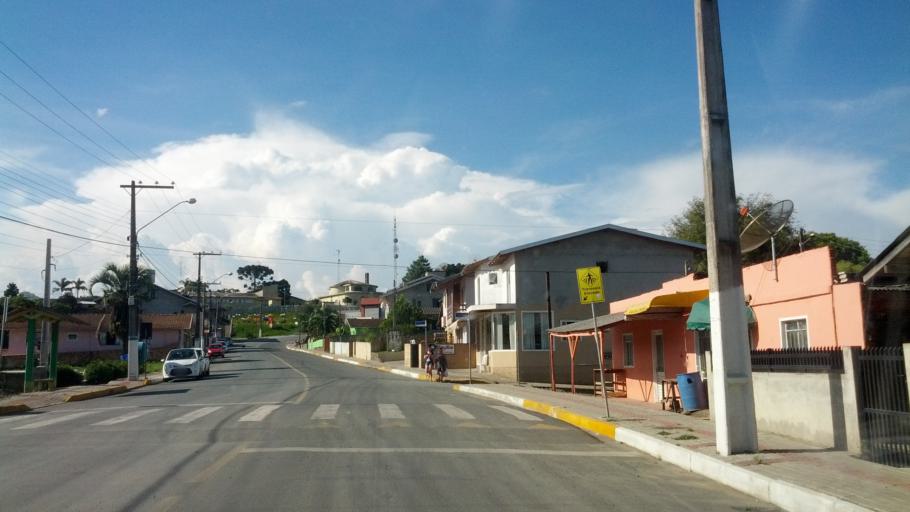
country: BR
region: Santa Catarina
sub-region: Otacilio Costa
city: Otacilio Costa
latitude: -27.4884
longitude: -50.1218
